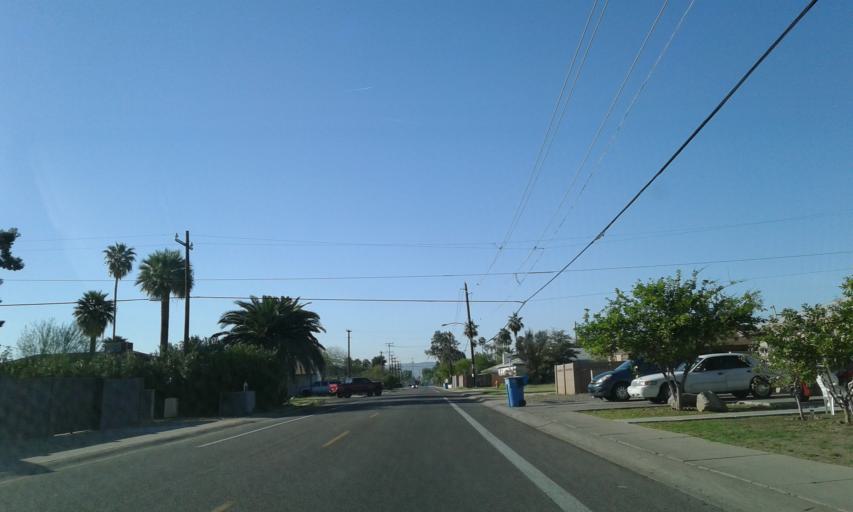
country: US
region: Arizona
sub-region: Maricopa County
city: Phoenix
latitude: 33.4847
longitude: -112.1085
